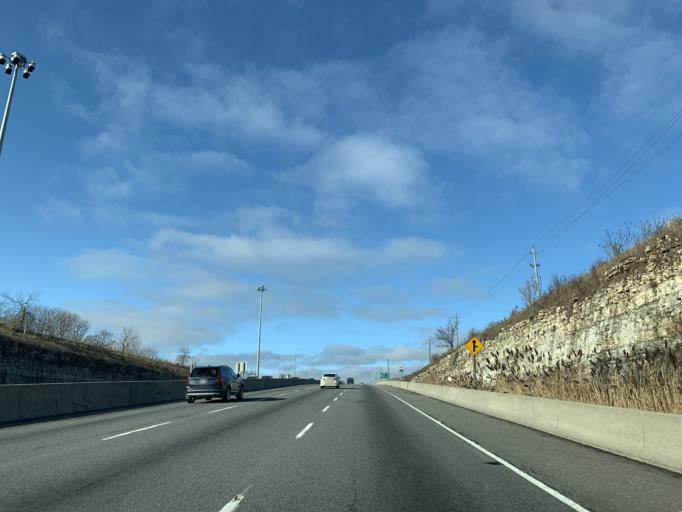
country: CA
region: Ontario
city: Hamilton
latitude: 43.3089
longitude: -79.9130
